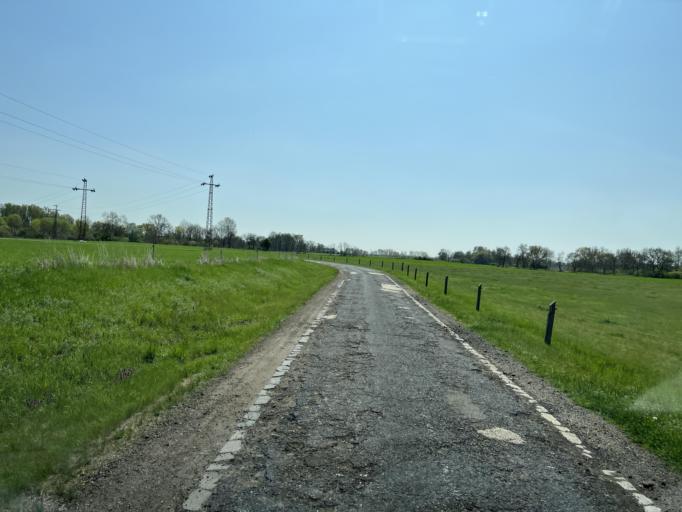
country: HU
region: Pest
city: Inarcs
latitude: 47.2577
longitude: 19.2816
